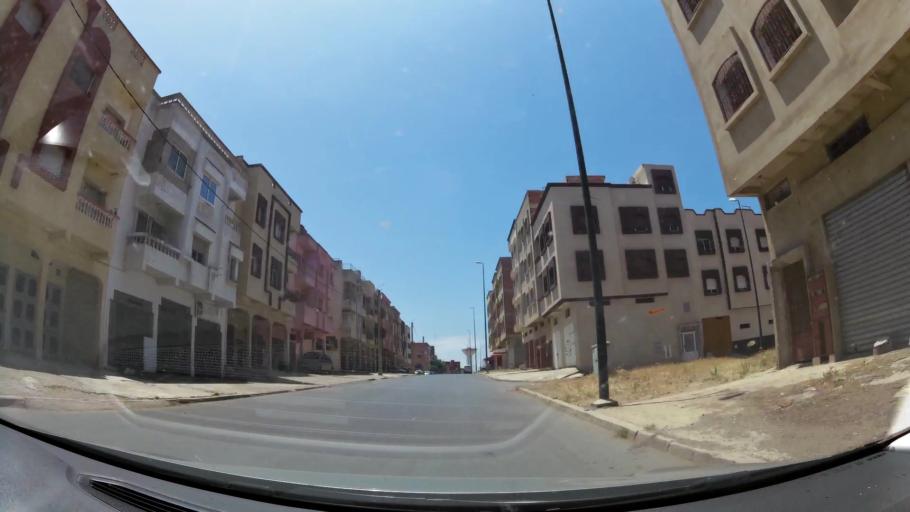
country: MA
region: Gharb-Chrarda-Beni Hssen
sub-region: Kenitra Province
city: Kenitra
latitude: 34.2597
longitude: -6.6259
